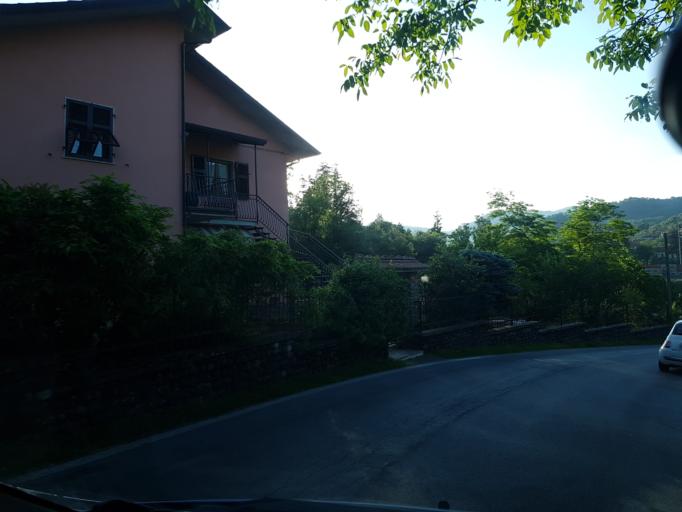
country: IT
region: Tuscany
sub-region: Provincia di Massa-Carrara
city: Casola in Lunigiana
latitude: 44.1924
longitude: 10.1965
